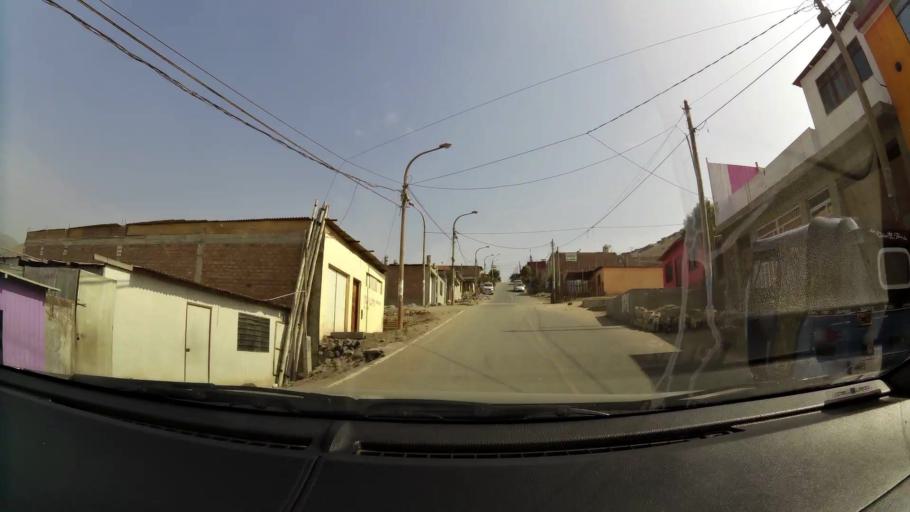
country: PE
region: Lima
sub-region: Lima
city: Santa Rosa
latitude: -11.7846
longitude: -77.1636
